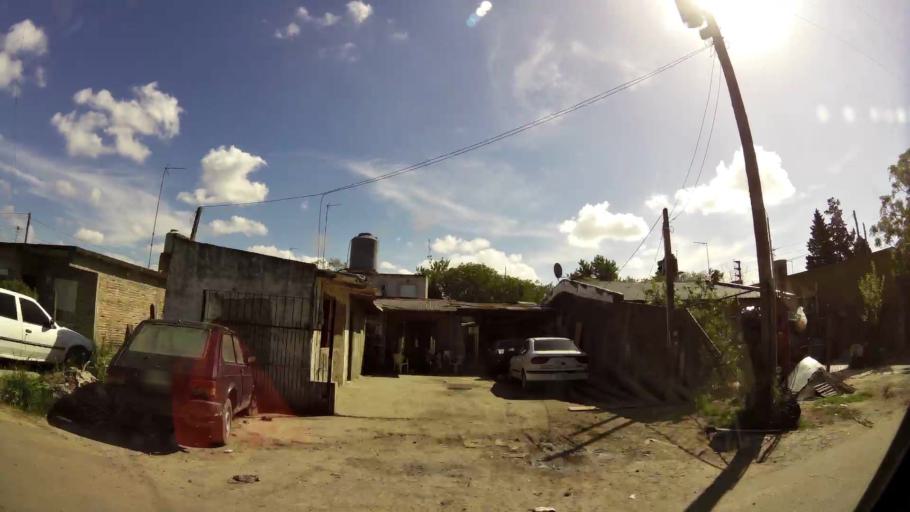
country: AR
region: Buenos Aires
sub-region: Partido de Quilmes
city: Quilmes
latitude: -34.7991
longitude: -58.2476
